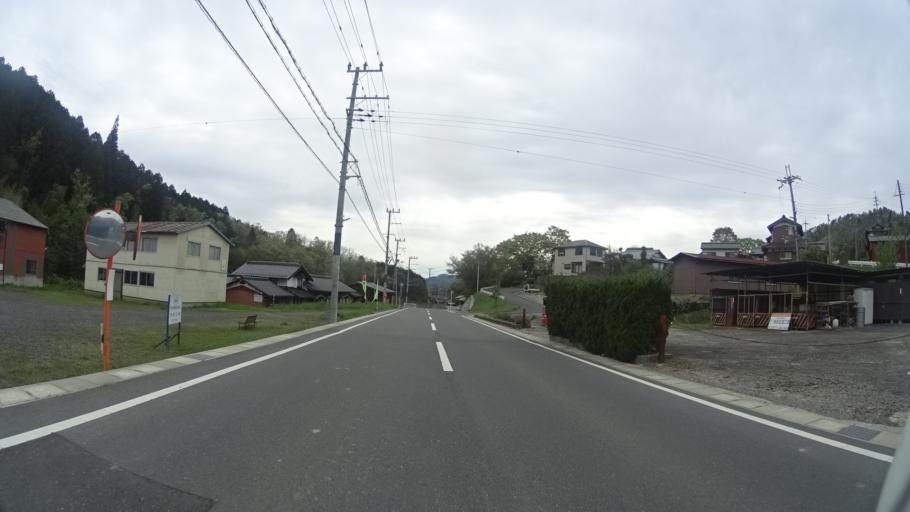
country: JP
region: Kyoto
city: Kameoka
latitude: 35.1810
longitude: 135.4480
